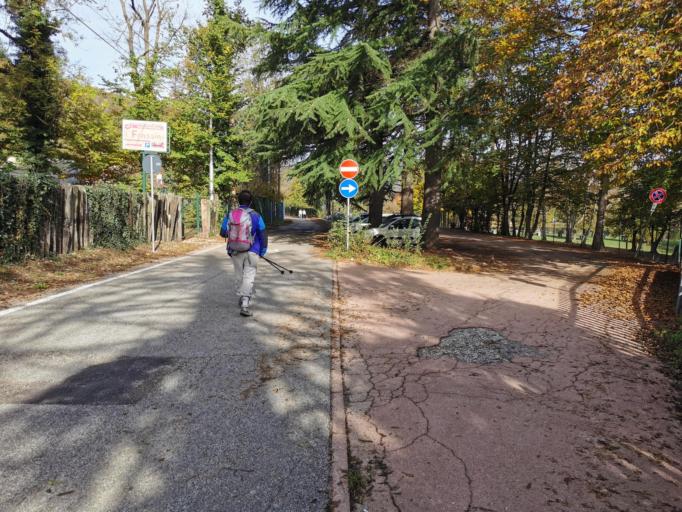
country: IT
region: Lombardy
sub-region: Provincia di Varese
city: Valganna
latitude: 45.9180
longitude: 8.8199
